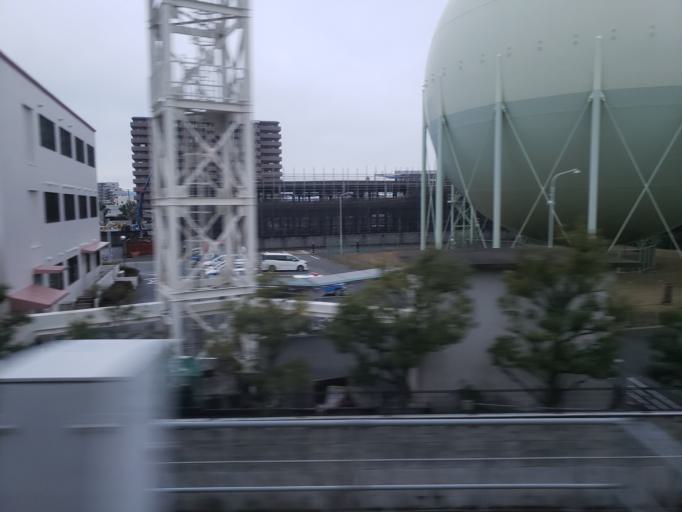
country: JP
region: Hyogo
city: Akashi
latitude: 34.6546
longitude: 134.9771
